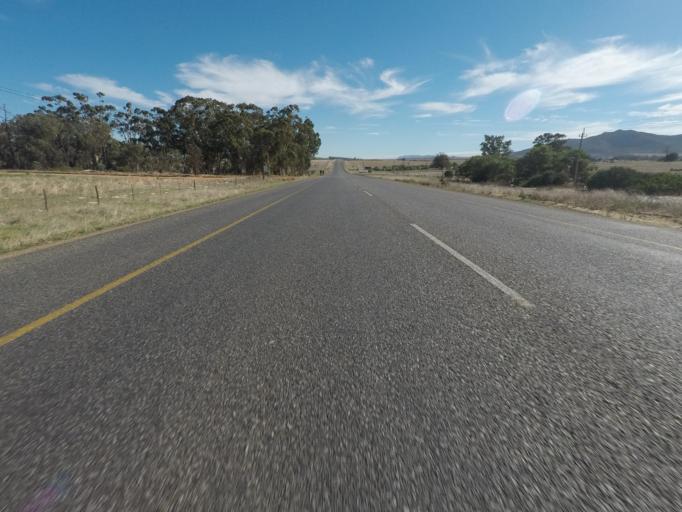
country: ZA
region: Western Cape
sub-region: West Coast District Municipality
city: Malmesbury
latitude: -33.6167
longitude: 18.7267
